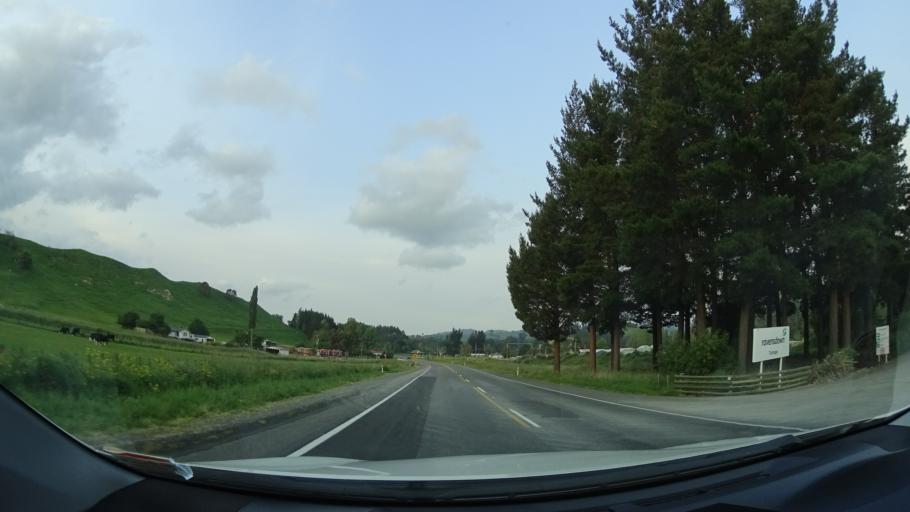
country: NZ
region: Manawatu-Wanganui
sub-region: Ruapehu District
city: Waiouru
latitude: -39.7357
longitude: 175.8419
